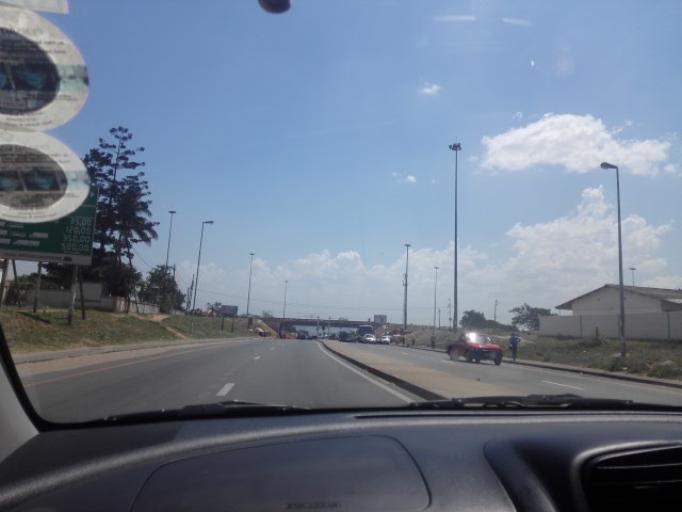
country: MZ
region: Maputo City
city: Maputo
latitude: -25.9425
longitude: 32.5429
